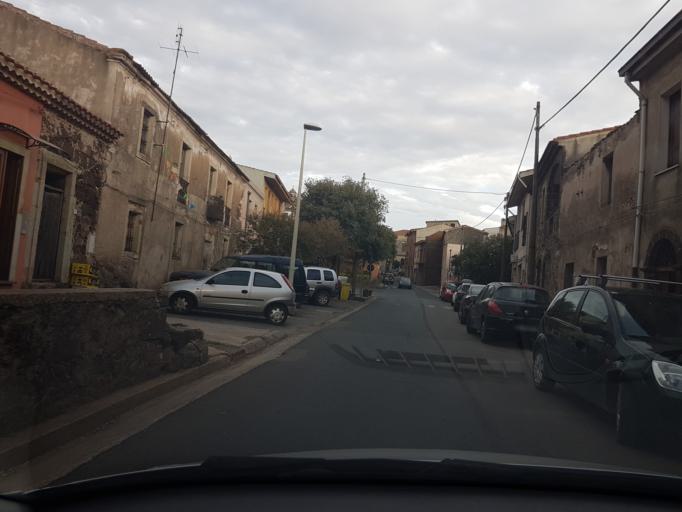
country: IT
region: Sardinia
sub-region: Provincia di Oristano
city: Seneghe
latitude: 40.0815
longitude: 8.6102
